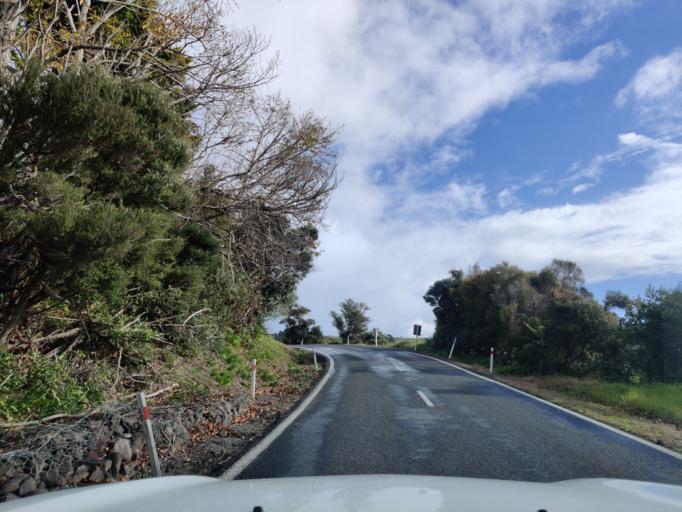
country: NZ
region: Waikato
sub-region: Thames-Coromandel District
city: Coromandel
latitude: -36.8087
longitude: 175.4936
